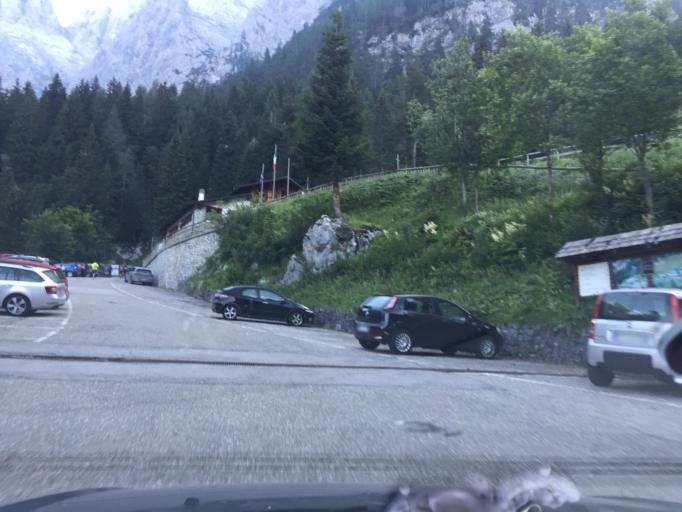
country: IT
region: Friuli Venezia Giulia
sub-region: Provincia di Udine
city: Rigolato
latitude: 46.5914
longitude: 12.8675
